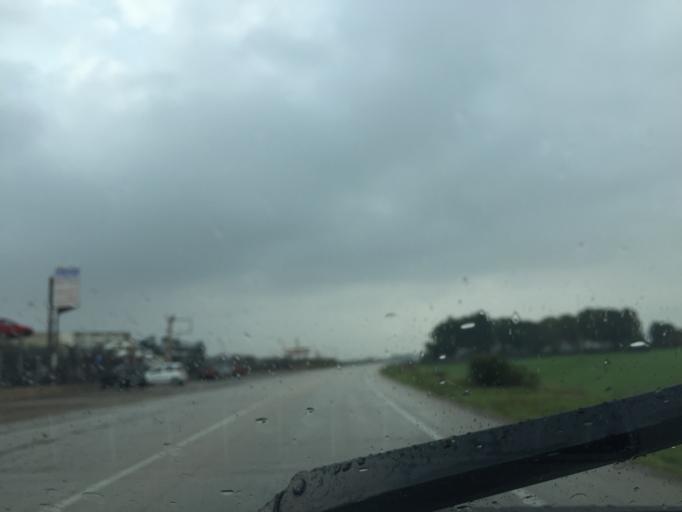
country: IT
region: Apulia
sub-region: Provincia di Foggia
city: Foggia
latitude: 41.4871
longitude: 15.5225
